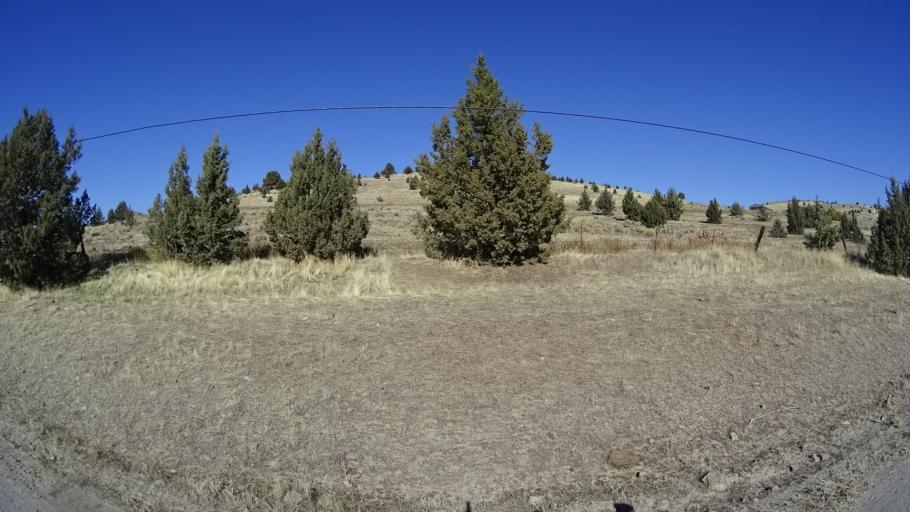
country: US
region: California
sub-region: Siskiyou County
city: Montague
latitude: 41.7281
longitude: -122.3656
